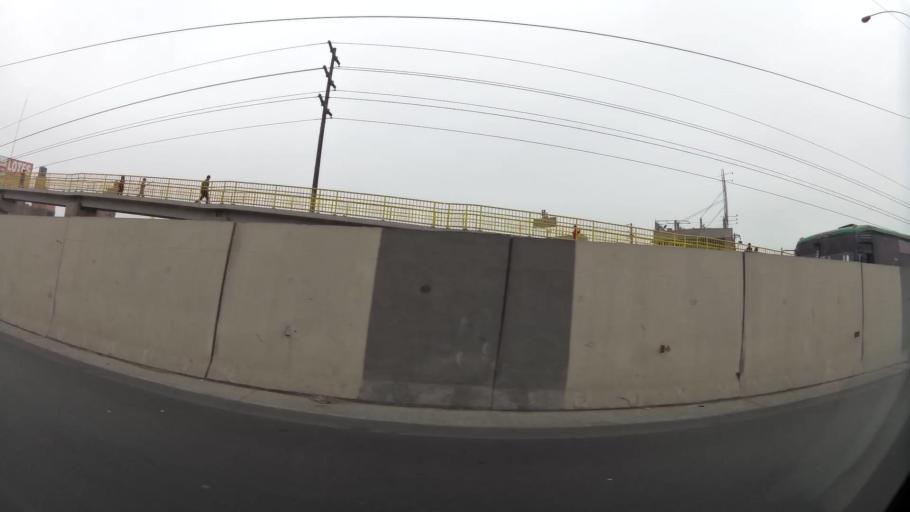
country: PE
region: Lima
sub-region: Lima
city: Urb. Santo Domingo
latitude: -11.8854
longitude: -77.0686
